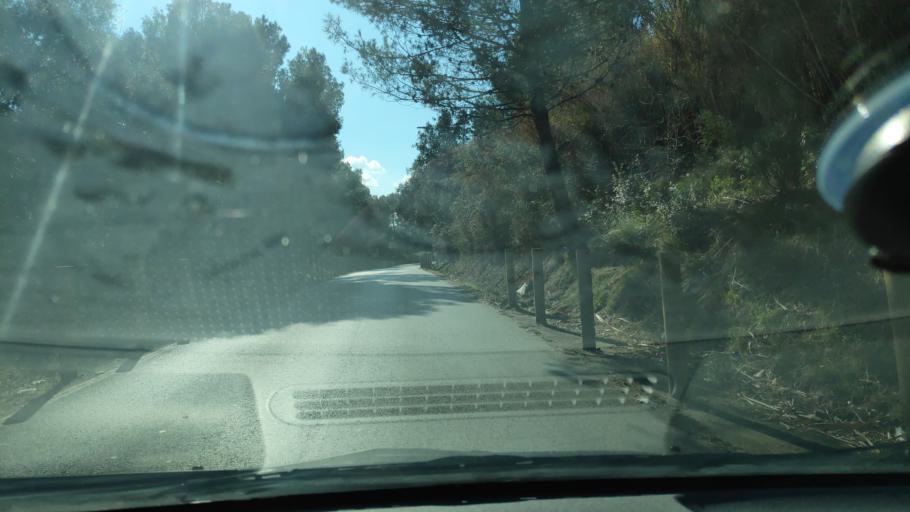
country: ES
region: Catalonia
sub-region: Provincia de Barcelona
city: Sant Quirze del Valles
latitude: 41.5566
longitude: 2.0558
